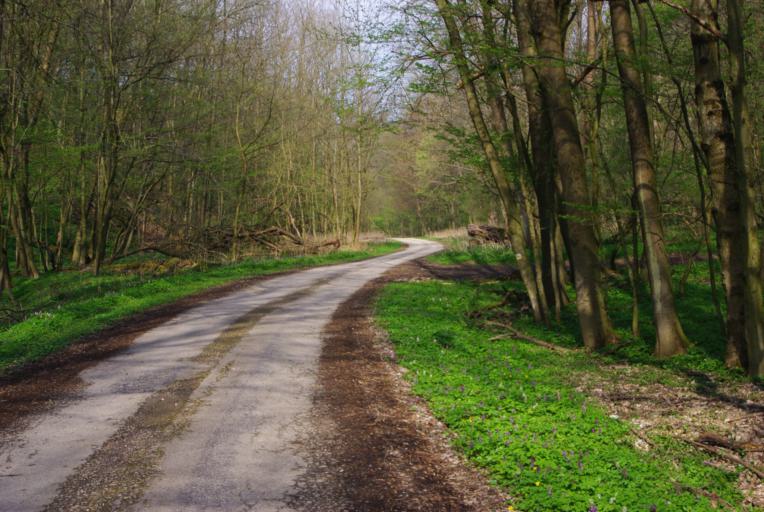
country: HU
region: Fejer
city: Szarliget
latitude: 47.4622
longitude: 18.4493
